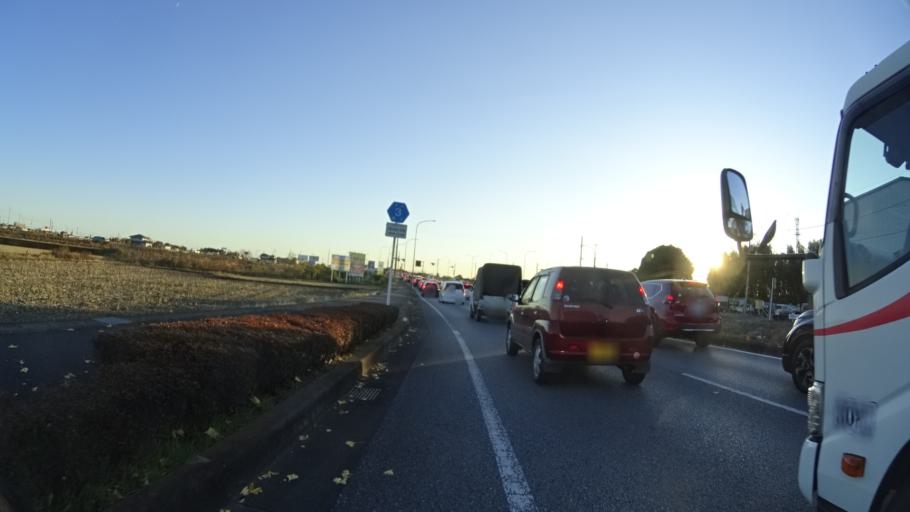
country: JP
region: Tochigi
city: Utsunomiya-shi
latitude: 36.5223
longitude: 139.8415
